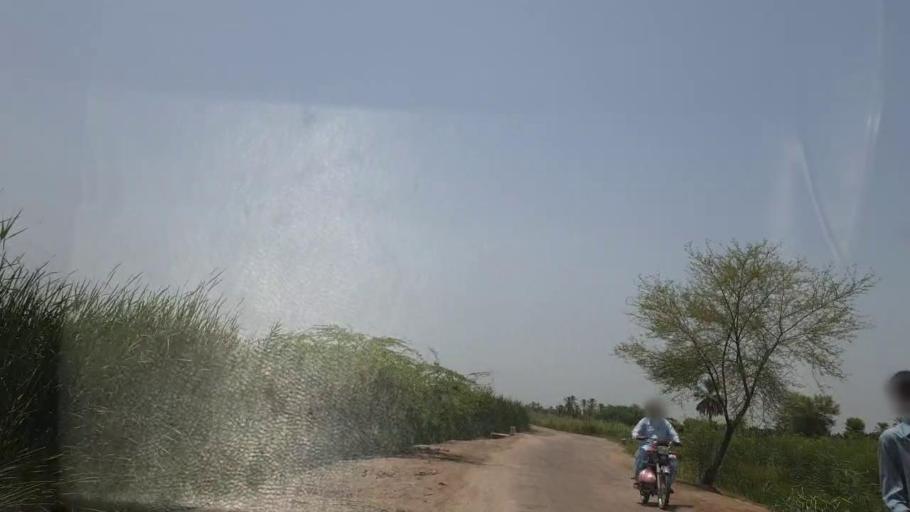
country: PK
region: Sindh
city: Bozdar
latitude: 27.2488
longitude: 68.6578
